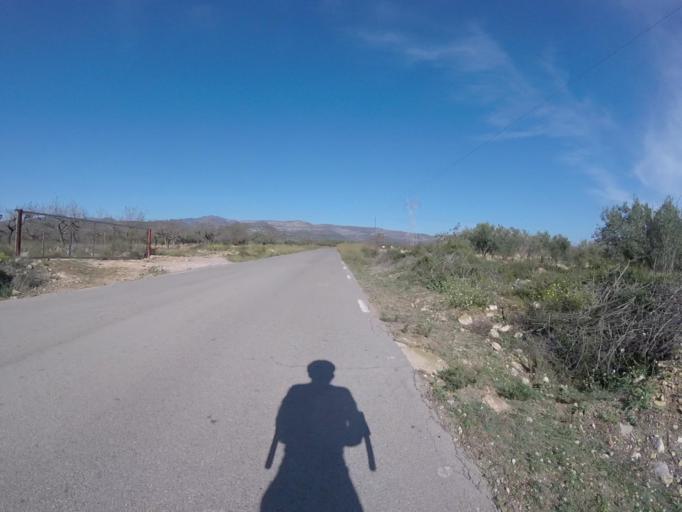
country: ES
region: Valencia
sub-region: Provincia de Castello
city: Sarratella
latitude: 40.2650
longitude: 0.0666
